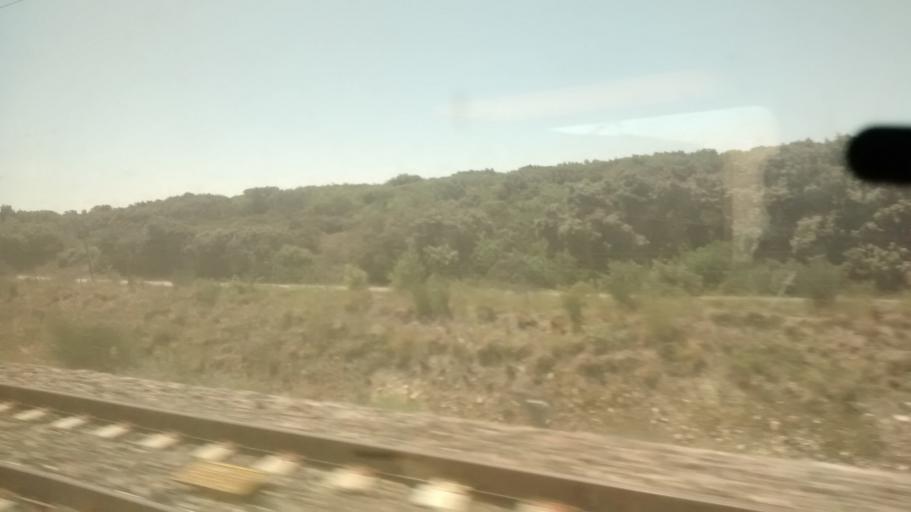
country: FR
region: Languedoc-Roussillon
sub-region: Departement du Gard
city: Pujaut
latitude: 44.0185
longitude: 4.7422
